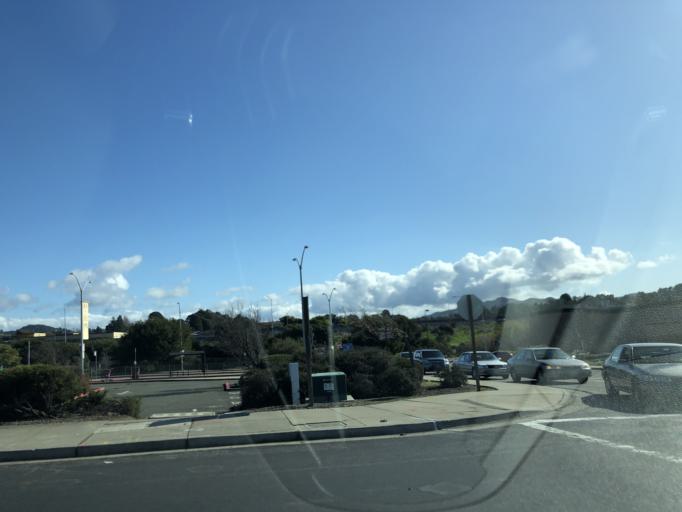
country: US
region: California
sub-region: Contra Costa County
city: Tara Hills
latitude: 37.9860
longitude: -122.3177
